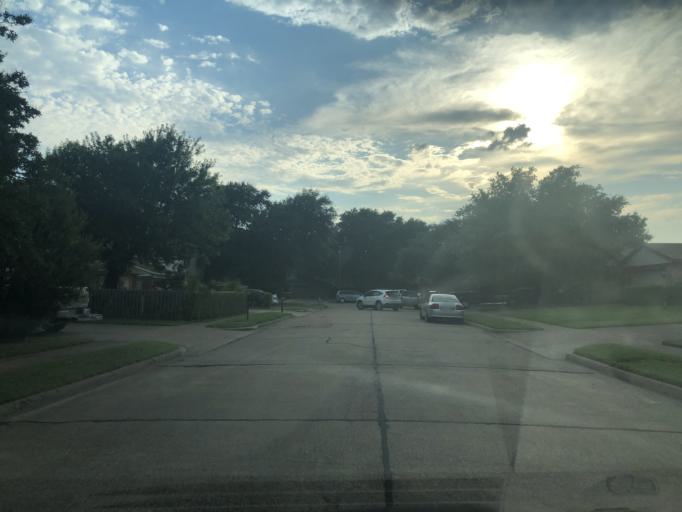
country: US
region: Texas
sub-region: Dallas County
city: Irving
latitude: 32.7917
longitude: -96.9518
